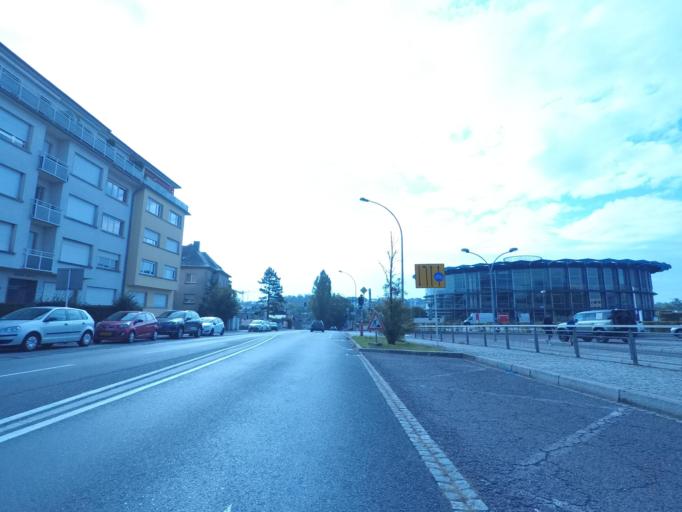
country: LU
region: Luxembourg
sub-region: Canton de Luxembourg
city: Luxembourg
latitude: 49.6018
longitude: 6.1138
